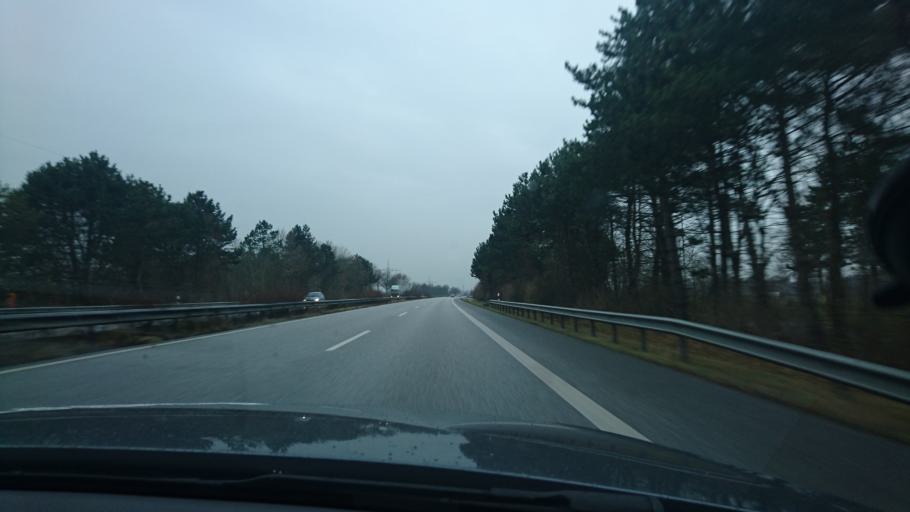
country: DE
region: Schleswig-Holstein
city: Lensahn
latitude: 54.2394
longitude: 10.8919
